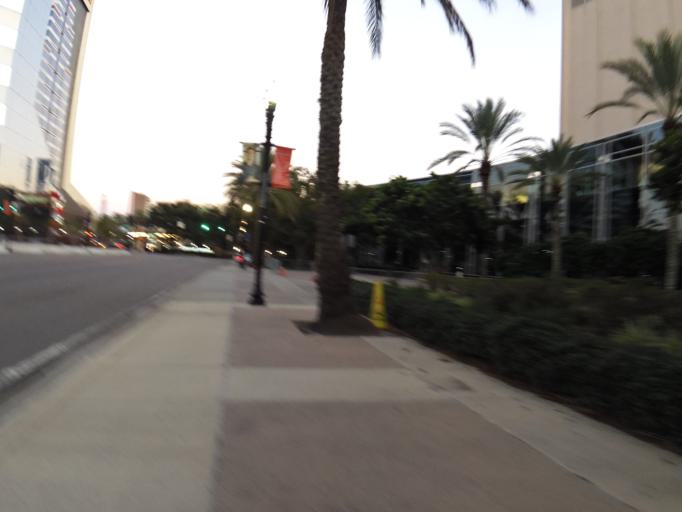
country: US
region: Florida
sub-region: Duval County
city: Jacksonville
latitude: 30.3255
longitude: -81.6623
